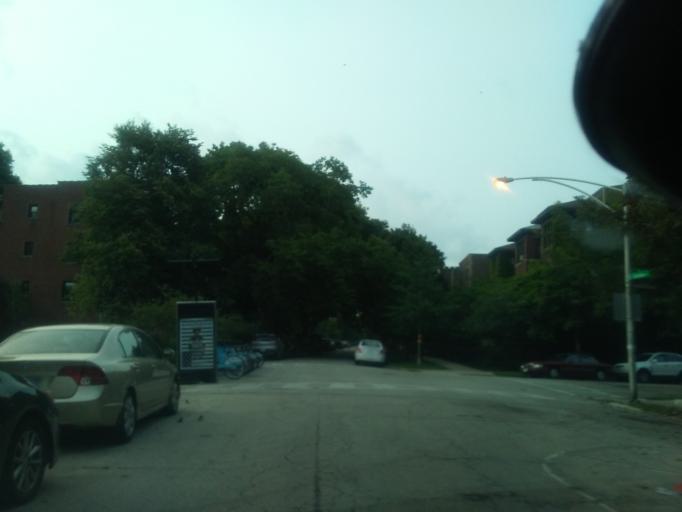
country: US
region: Illinois
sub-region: Cook County
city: Evanston
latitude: 42.0210
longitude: -87.6652
